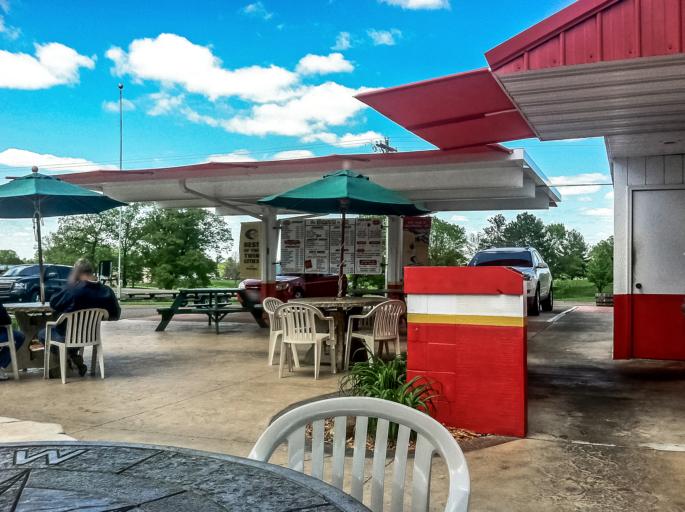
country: US
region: Wisconsin
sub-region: Burnett County
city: Grantsburg
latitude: 45.7724
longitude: -92.6839
